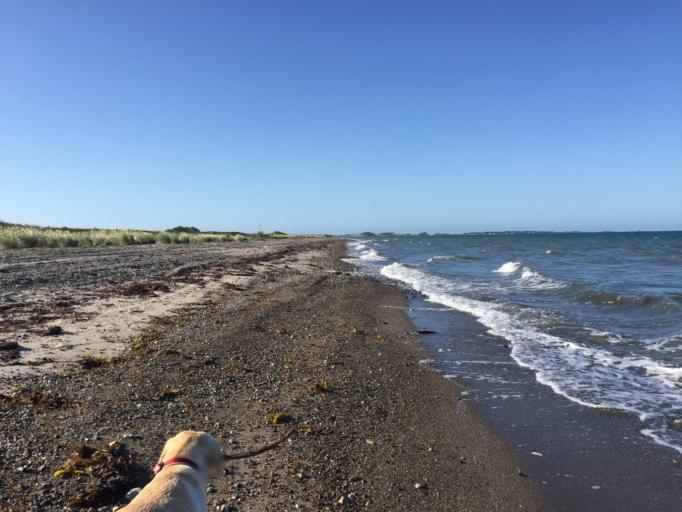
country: DK
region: Zealand
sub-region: Slagelse Kommune
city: Korsor
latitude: 55.2092
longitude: 11.1729
